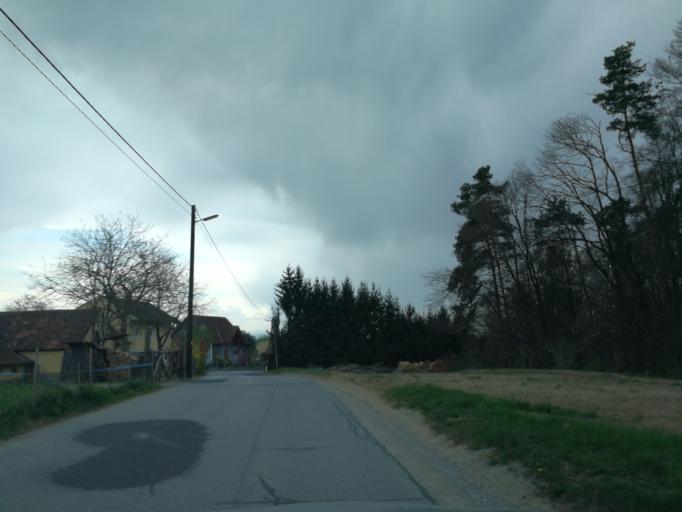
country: AT
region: Styria
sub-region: Politischer Bezirk Graz-Umgebung
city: Hart bei Graz
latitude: 47.0623
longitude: 15.5043
